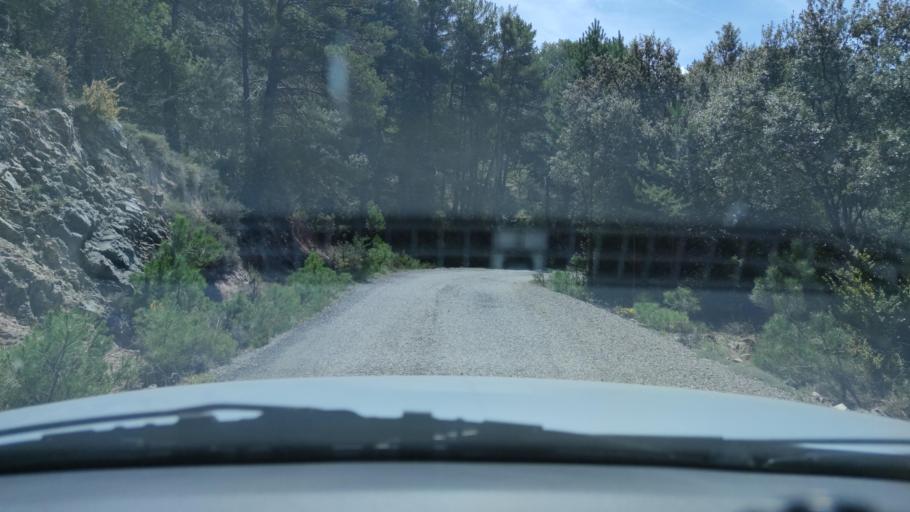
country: ES
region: Catalonia
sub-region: Provincia de Lleida
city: Sort
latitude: 42.3205
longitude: 1.0902
